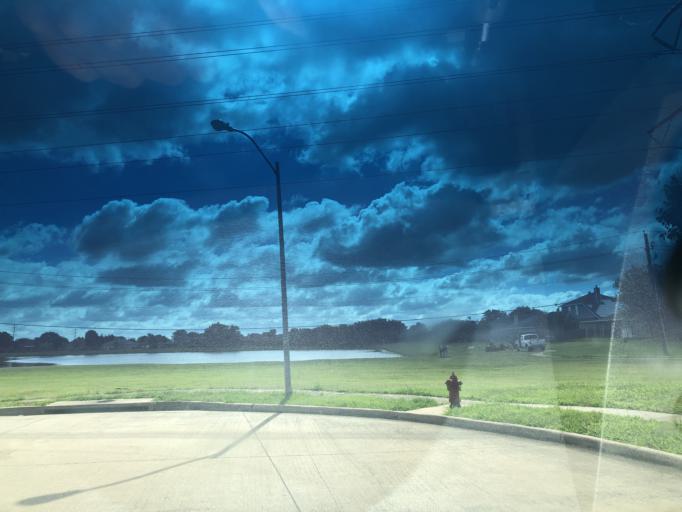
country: US
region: Texas
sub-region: Dallas County
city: Grand Prairie
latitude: 32.6935
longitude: -97.0350
